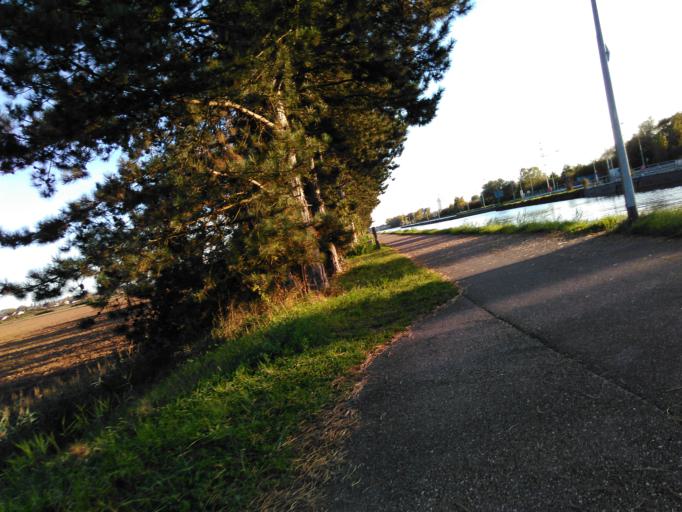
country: FR
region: Lorraine
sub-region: Departement de la Moselle
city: Talange
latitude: 49.2279
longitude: 6.1837
